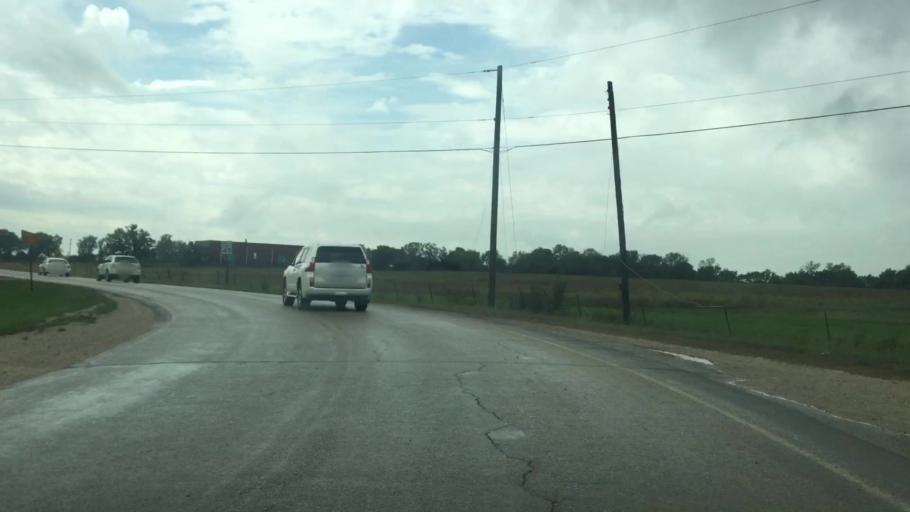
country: US
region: Kansas
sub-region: Allen County
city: Iola
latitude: 37.8898
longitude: -95.4093
